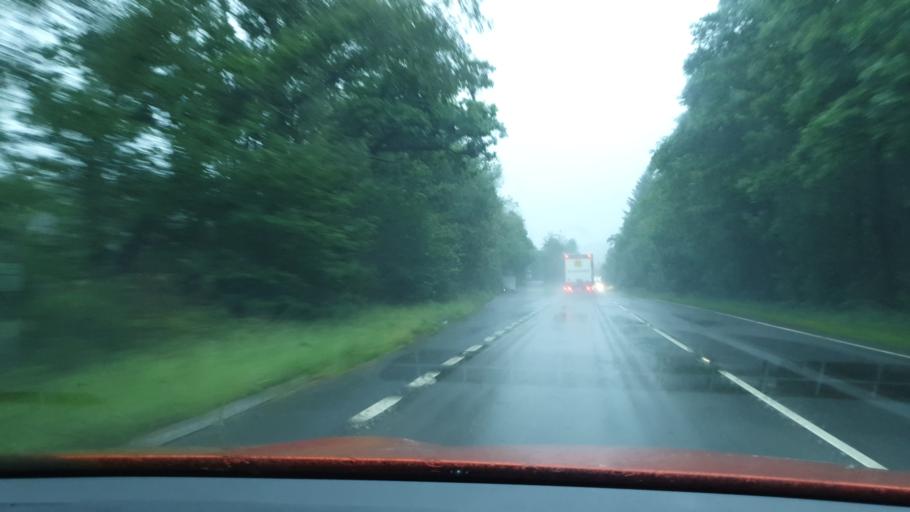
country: GB
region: England
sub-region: Cumbria
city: Ulverston
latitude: 54.2484
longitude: -3.0382
